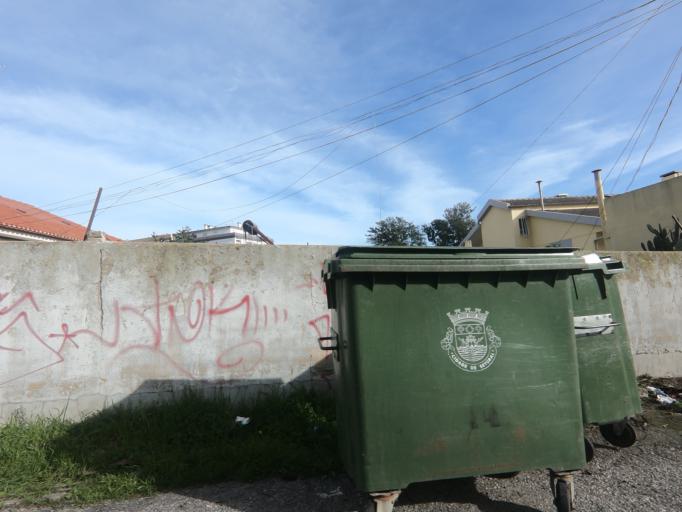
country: PT
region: Setubal
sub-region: Setubal
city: Setubal
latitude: 38.5299
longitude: -8.8991
